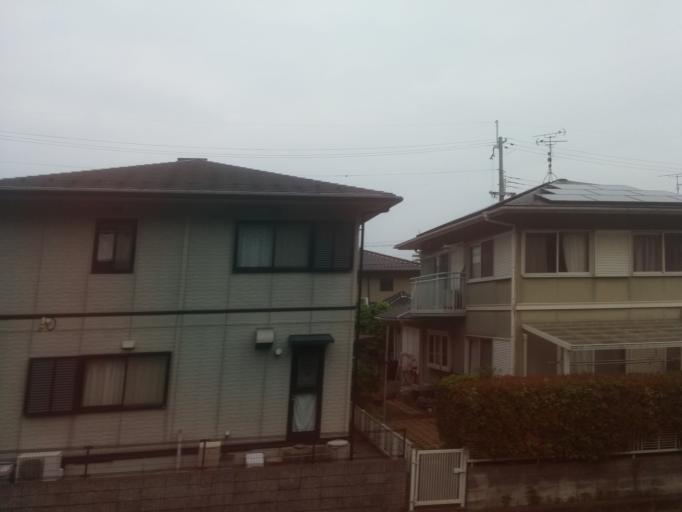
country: JP
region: Shiga Prefecture
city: Youkaichi
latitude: 35.1745
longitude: 136.1602
